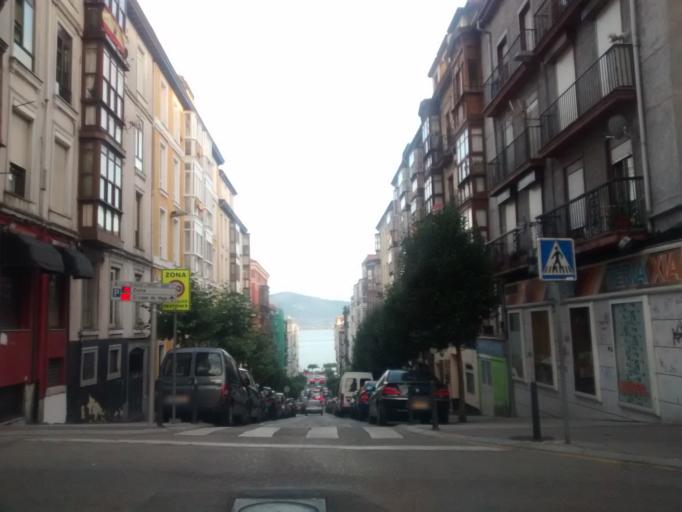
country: ES
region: Cantabria
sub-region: Provincia de Cantabria
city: Santander
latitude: 43.4644
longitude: -3.7999
